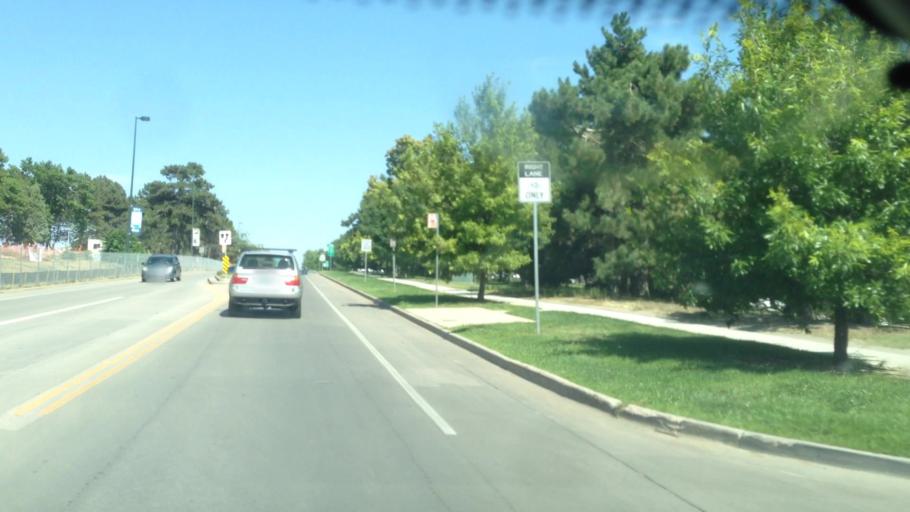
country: US
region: Colorado
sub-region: Denver County
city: Denver
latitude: 39.7512
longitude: -104.9488
